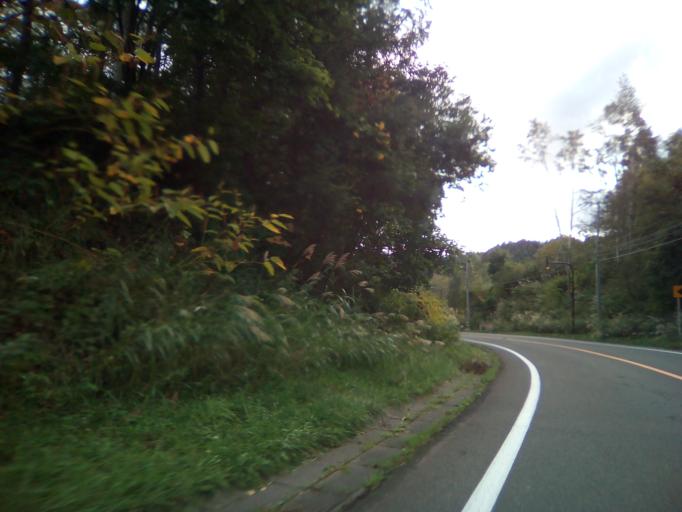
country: JP
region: Hokkaido
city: Niseko Town
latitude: 42.6613
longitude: 140.8251
